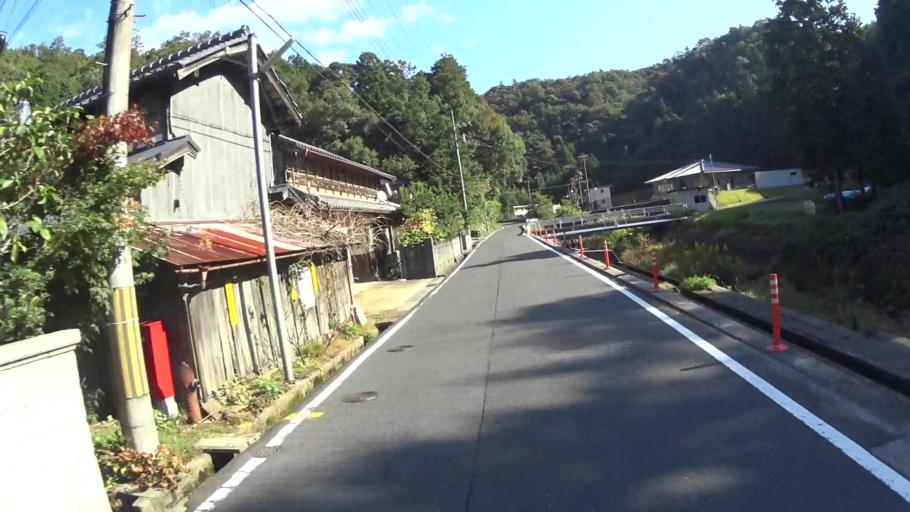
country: JP
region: Kyoto
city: Miyazu
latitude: 35.5771
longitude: 135.1603
